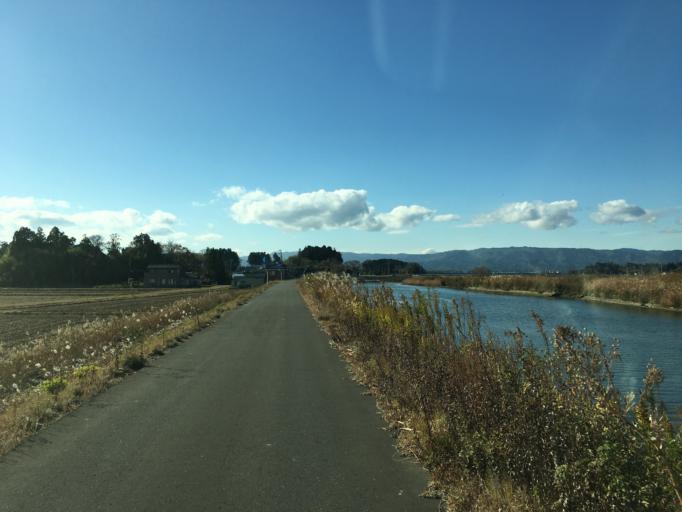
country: JP
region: Miyagi
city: Marumori
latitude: 37.8093
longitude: 140.9649
